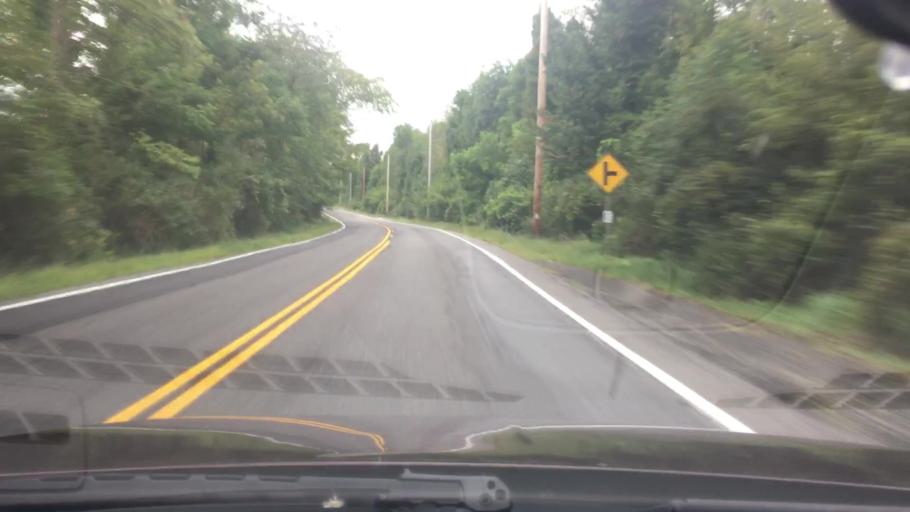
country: US
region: New York
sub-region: Dutchess County
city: Millbrook
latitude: 41.7929
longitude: -73.7174
